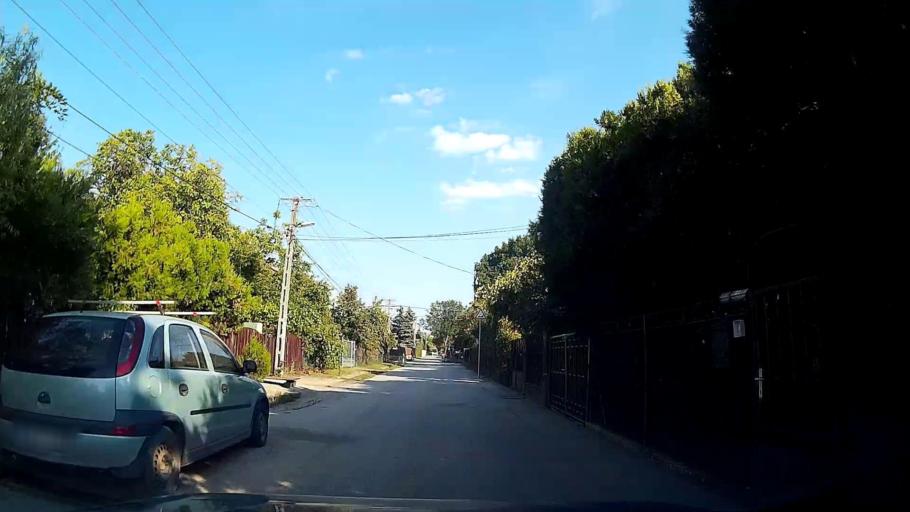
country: HU
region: Pest
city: Szentendre
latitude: 47.6503
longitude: 19.0639
